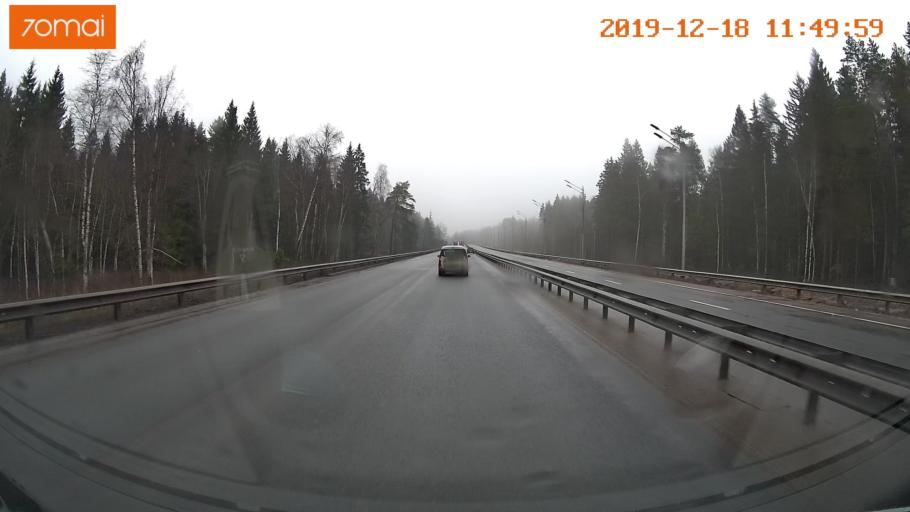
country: RU
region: Moskovskaya
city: Yershovo
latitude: 55.7822
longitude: 36.9156
